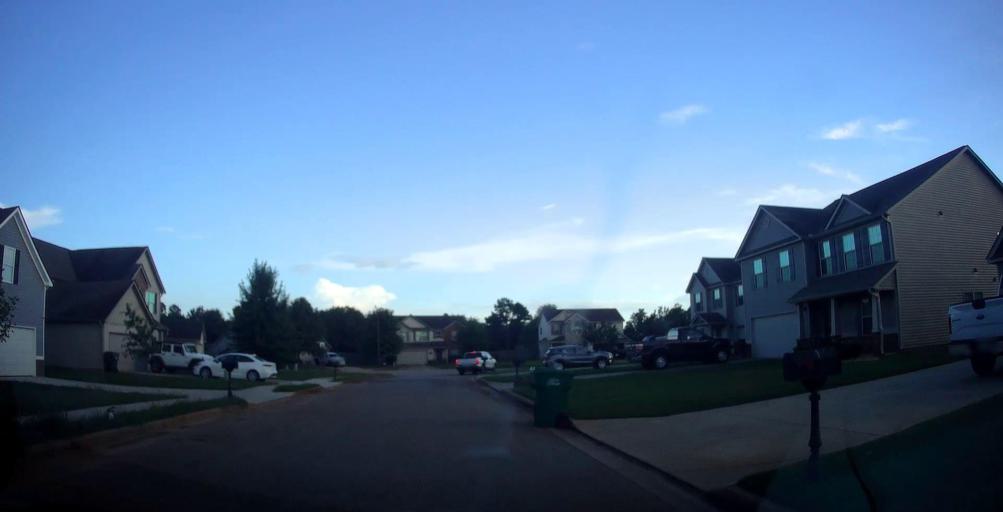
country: US
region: Georgia
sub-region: Houston County
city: Centerville
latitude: 32.6447
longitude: -83.7101
